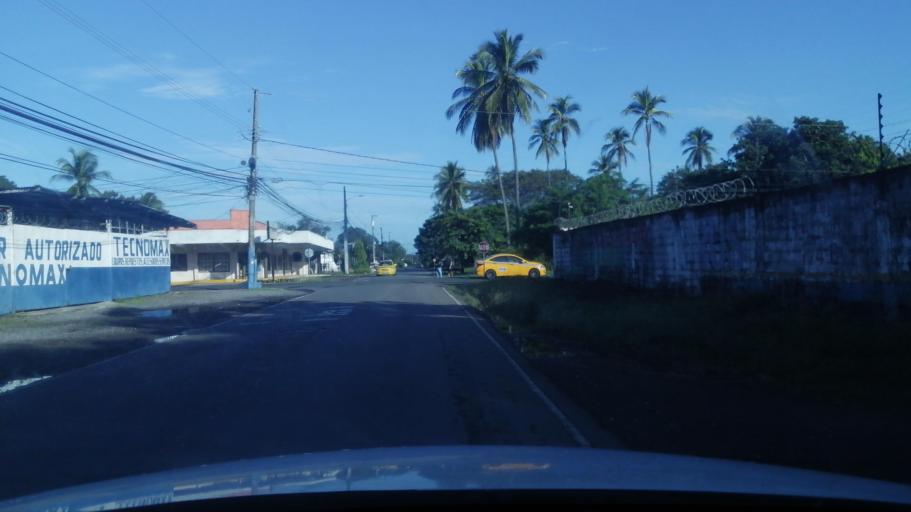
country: PA
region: Chiriqui
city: David
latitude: 8.4223
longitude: -82.4337
